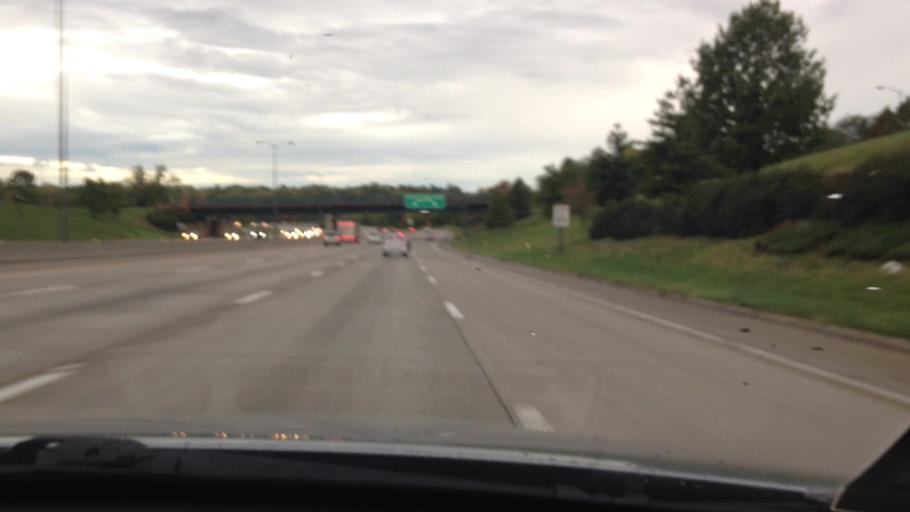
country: US
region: Missouri
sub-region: Jackson County
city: Kansas City
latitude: 39.0506
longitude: -94.5618
